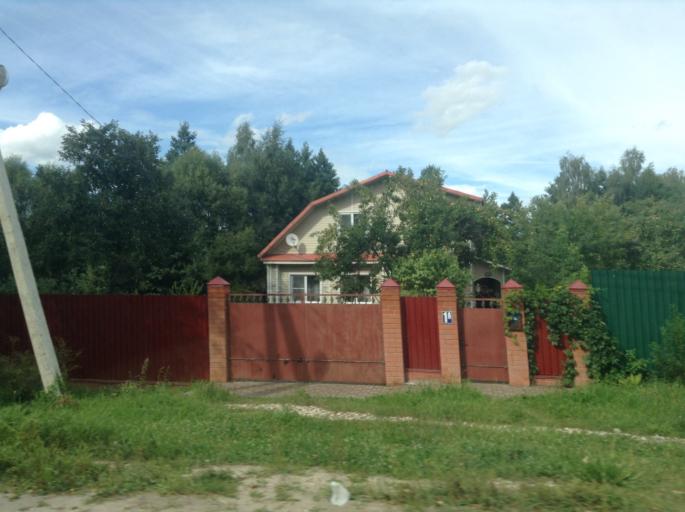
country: RU
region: Moskovskaya
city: Yegor'yevsk
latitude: 55.3601
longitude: 39.1081
